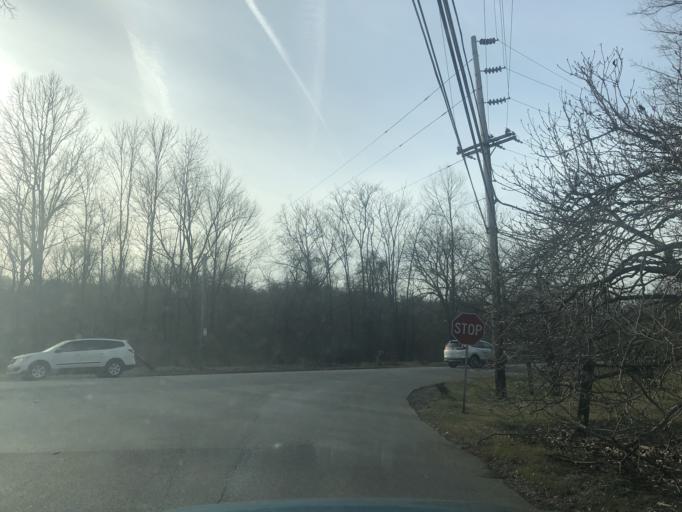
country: US
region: Pennsylvania
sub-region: Montgomery County
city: Fort Washington
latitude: 40.1238
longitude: -75.2191
